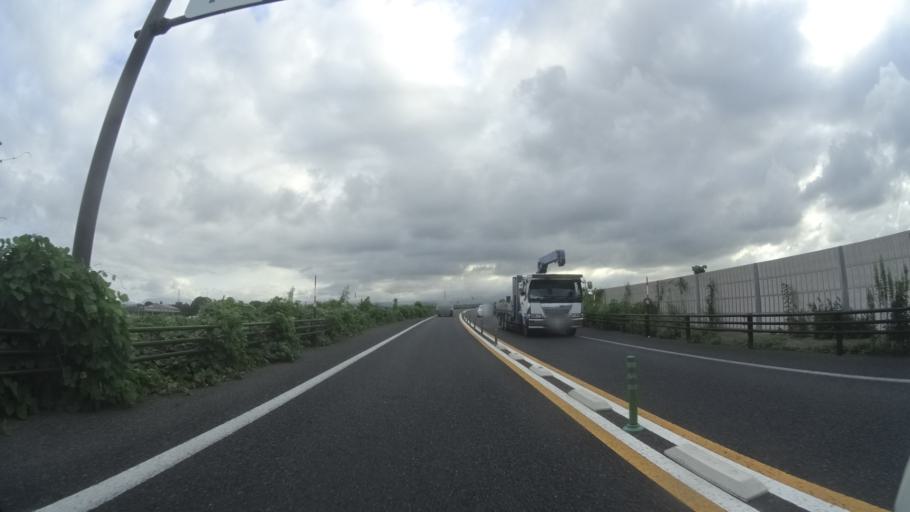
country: JP
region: Tottori
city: Kurayoshi
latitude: 35.4901
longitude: 133.7077
